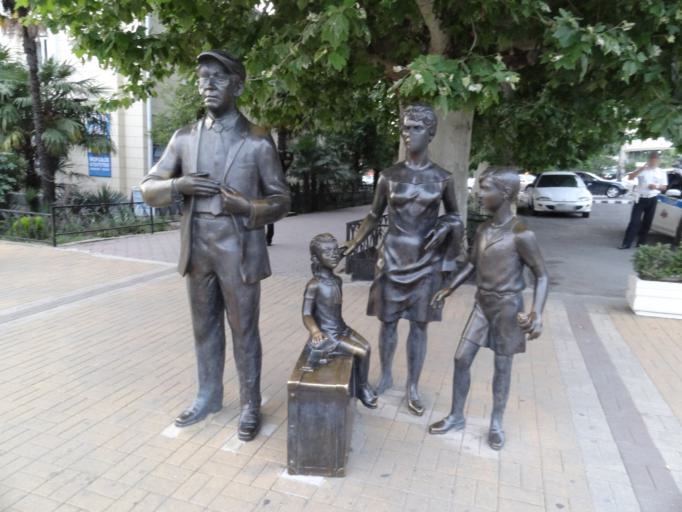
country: RU
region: Krasnodarskiy
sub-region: Sochi City
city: Sochi
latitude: 43.5802
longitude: 39.7195
